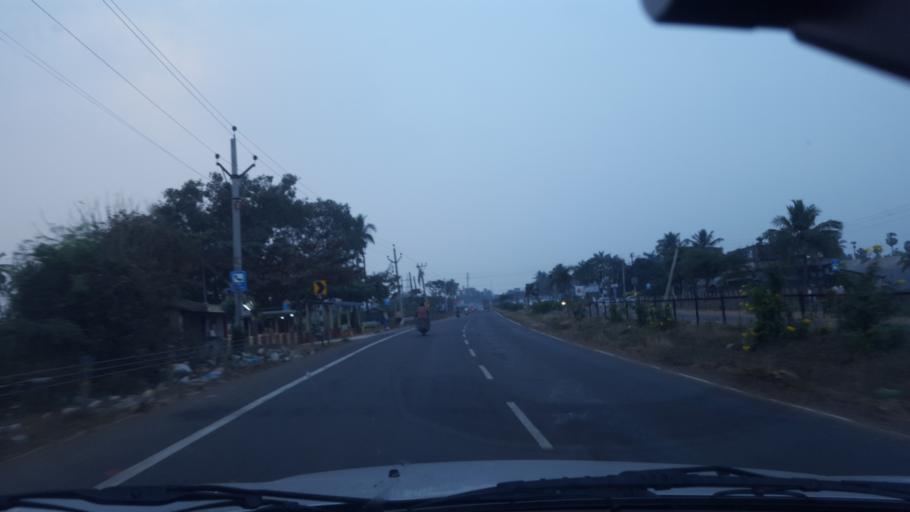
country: IN
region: Andhra Pradesh
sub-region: East Godavari
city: Rajahmundry
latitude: 16.8939
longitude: 81.7991
